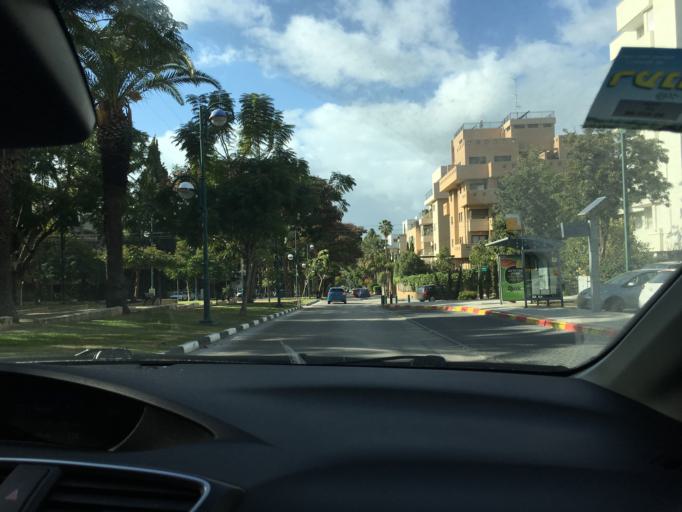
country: IL
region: Tel Aviv
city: Ramat HaSharon
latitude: 32.1446
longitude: 34.8432
